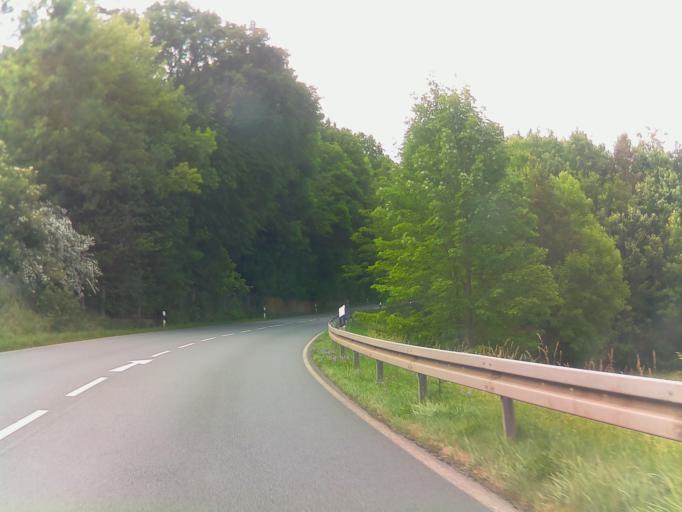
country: DE
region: Hesse
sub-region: Regierungsbezirk Kassel
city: Waldeck
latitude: 51.1972
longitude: 9.0864
